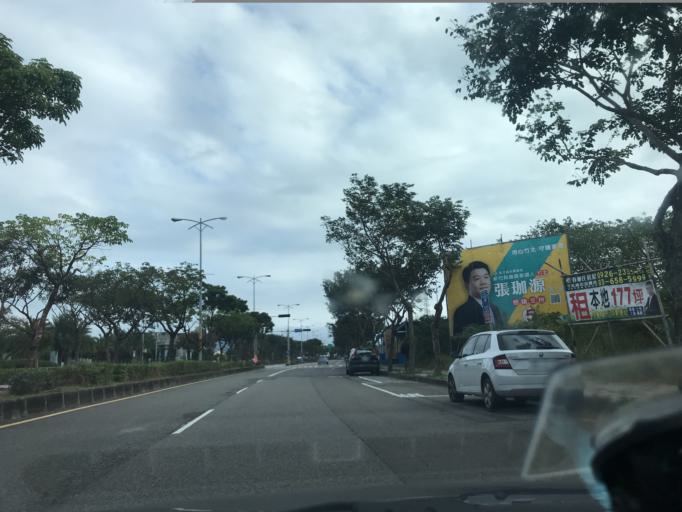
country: TW
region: Taiwan
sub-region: Hsinchu
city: Zhubei
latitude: 24.8049
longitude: 121.0430
